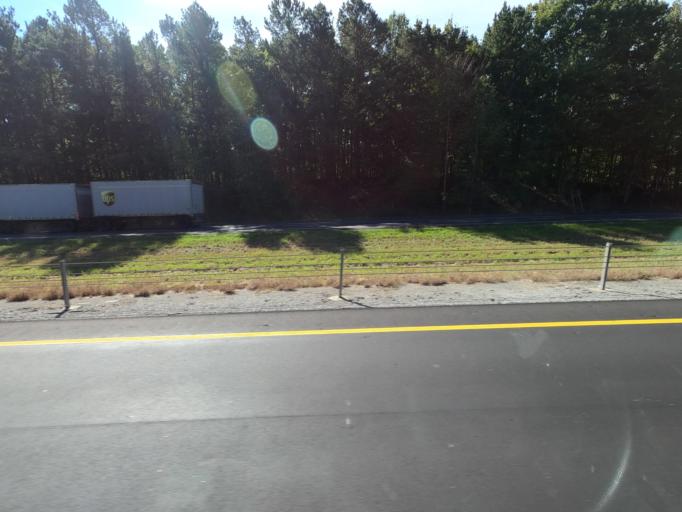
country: US
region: Tennessee
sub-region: Dickson County
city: Burns
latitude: 36.0189
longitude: -87.3451
